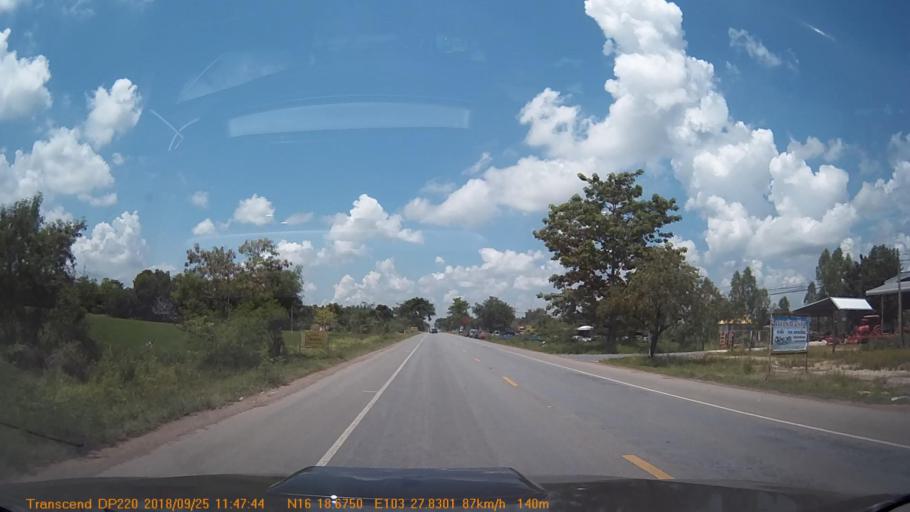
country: TH
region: Kalasin
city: Khong Chai
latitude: 16.3112
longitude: 103.4635
